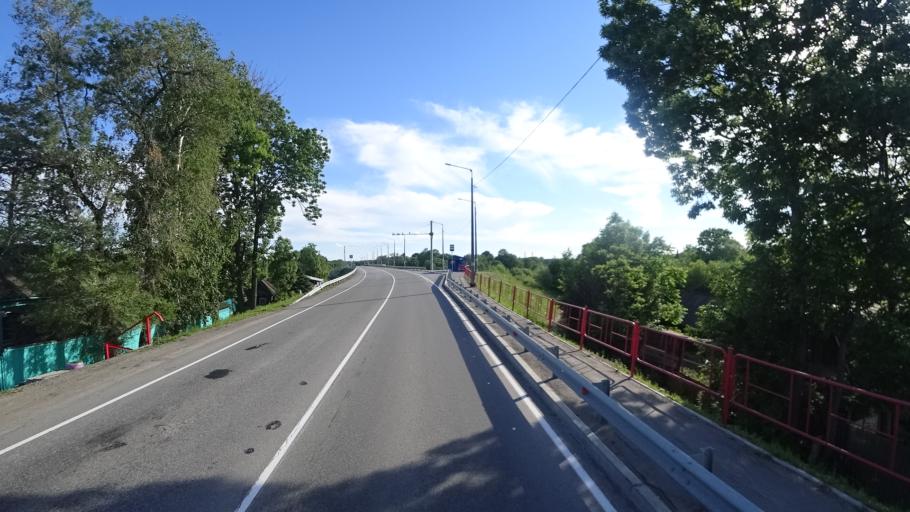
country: RU
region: Khabarovsk Krai
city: Khor
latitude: 47.8862
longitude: 134.9746
